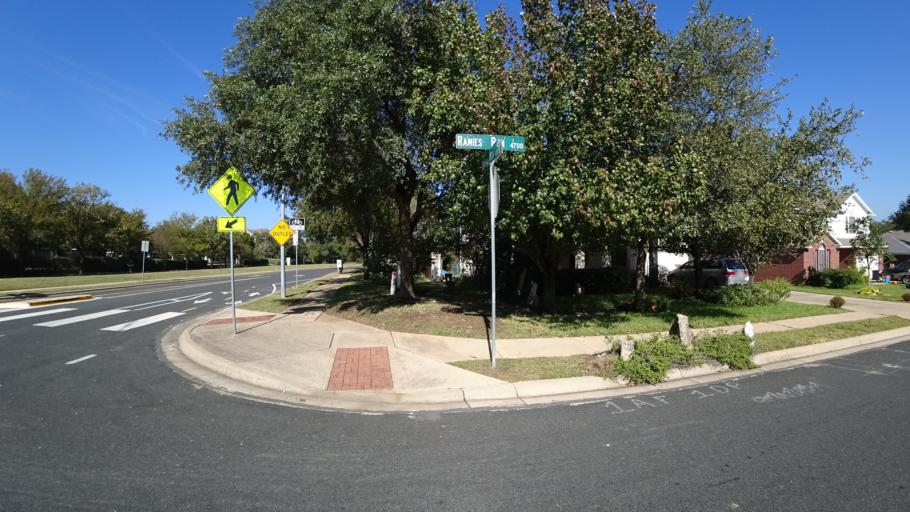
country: US
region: Texas
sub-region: Travis County
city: Shady Hollow
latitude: 30.2006
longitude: -97.8610
